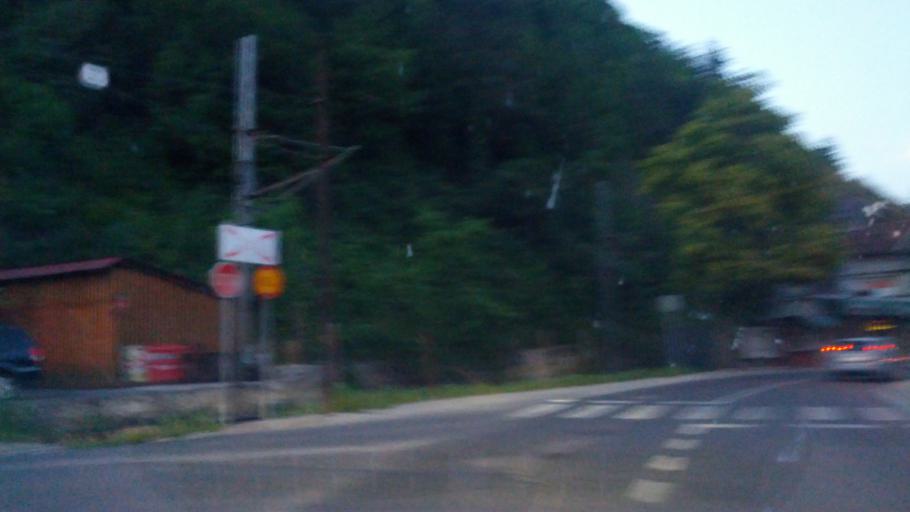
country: BA
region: Federation of Bosnia and Herzegovina
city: Bosanska Krupa
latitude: 44.8869
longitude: 16.1512
